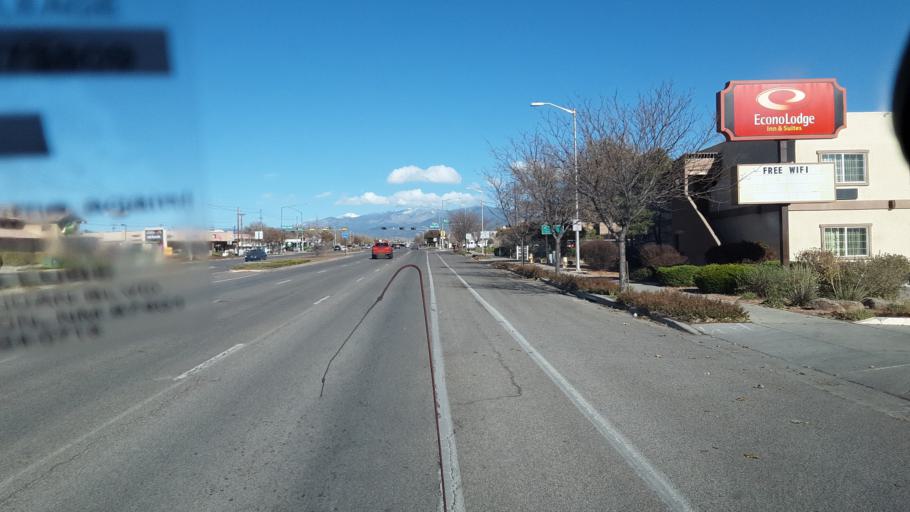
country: US
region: New Mexico
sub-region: Santa Fe County
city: Agua Fria
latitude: 35.6432
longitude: -106.0109
